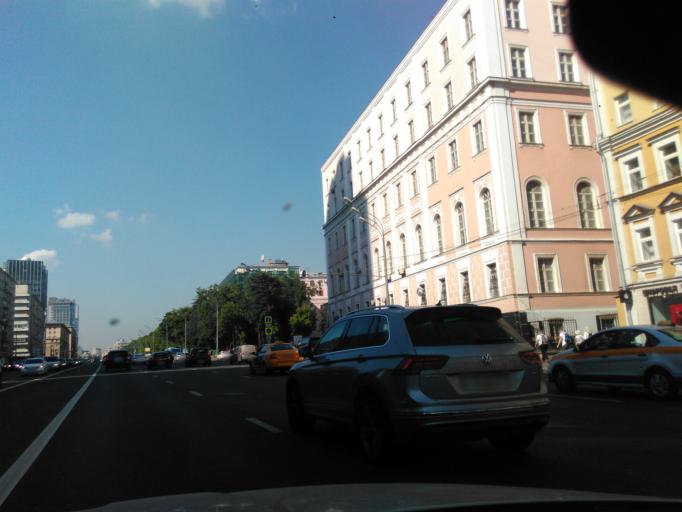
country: RU
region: Moscow
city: Moscow
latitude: 55.7279
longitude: 37.6079
